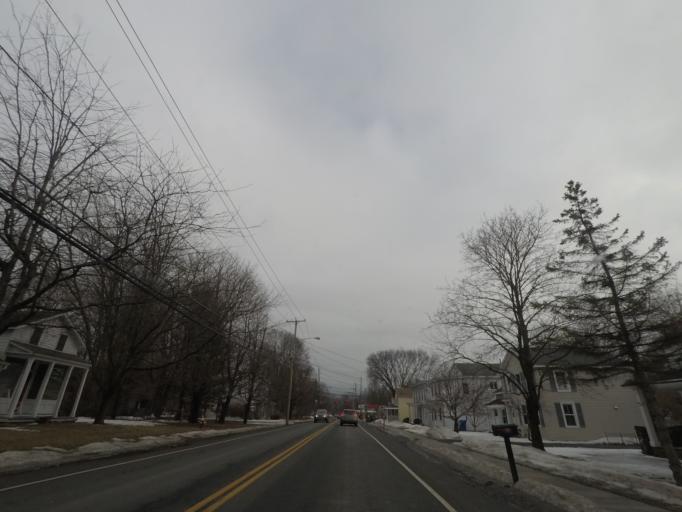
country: US
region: New York
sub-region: Albany County
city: Voorheesville
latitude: 42.7033
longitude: -73.9674
